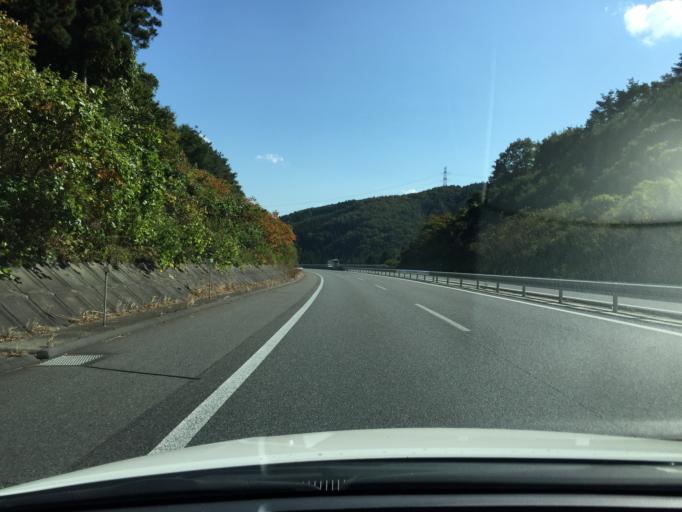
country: JP
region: Fukushima
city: Iwaki
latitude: 37.1565
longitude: 140.7331
